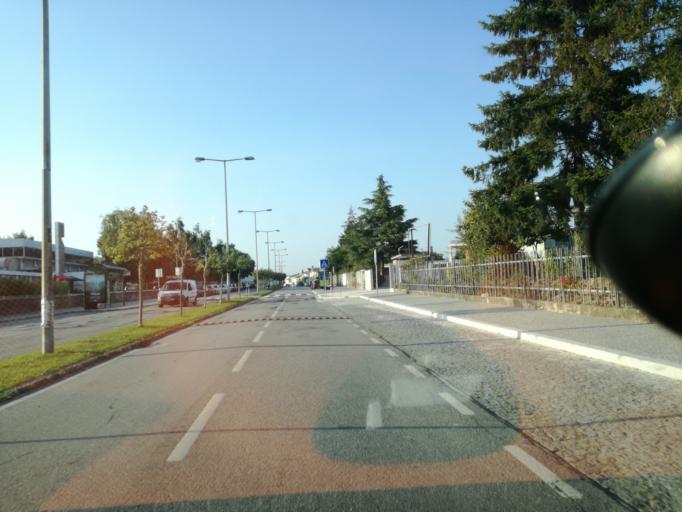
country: PT
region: Porto
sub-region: Maia
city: Milheiros
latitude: 41.2138
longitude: -8.6003
